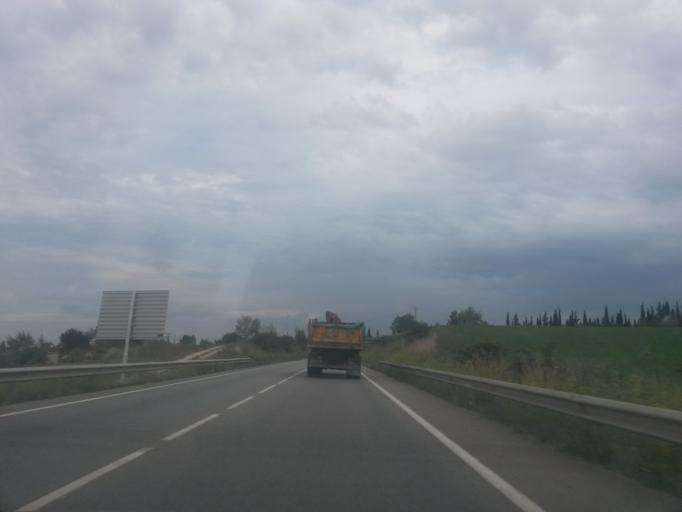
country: ES
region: Catalonia
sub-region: Provincia de Girona
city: Fontcoberta
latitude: 42.1186
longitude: 2.7875
